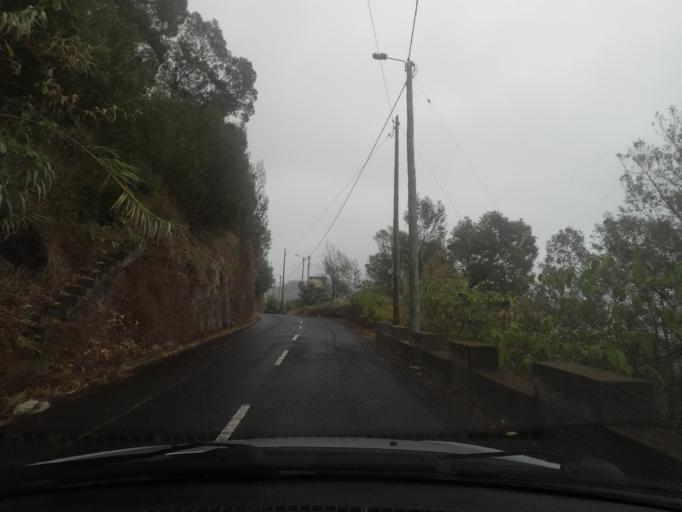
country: PT
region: Madeira
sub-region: Santana
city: Santana
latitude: 32.7824
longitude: -16.8581
